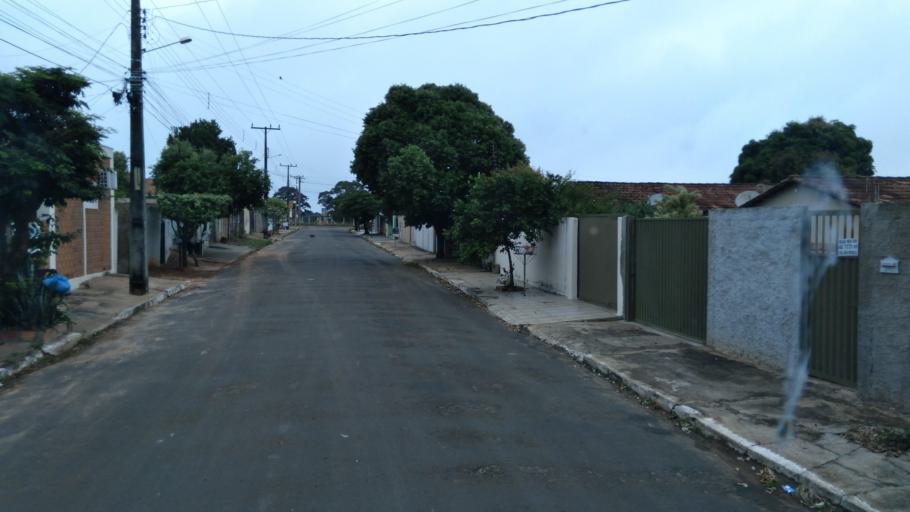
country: BR
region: Goias
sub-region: Mineiros
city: Mineiros
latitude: -17.5735
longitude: -52.5382
